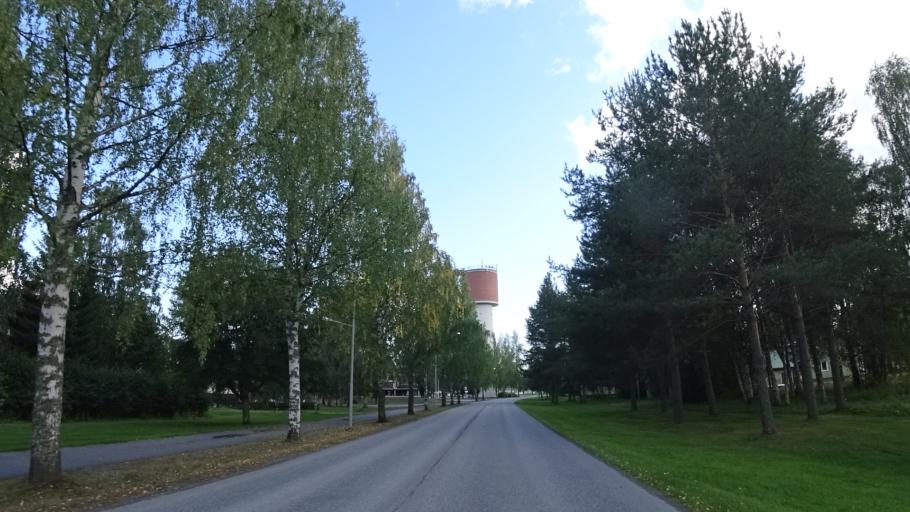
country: FI
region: North Karelia
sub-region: Pielisen Karjala
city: Lieksa
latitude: 63.3234
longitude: 30.0226
